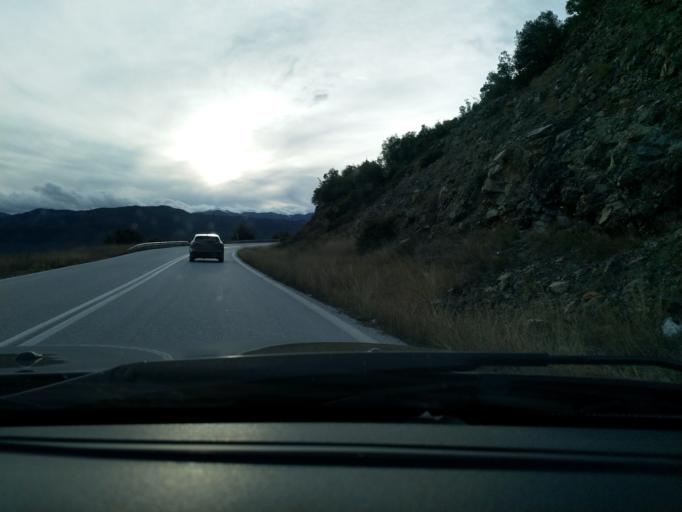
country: GR
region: Thessaly
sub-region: Trikala
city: Kastraki
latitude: 39.7724
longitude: 21.4549
